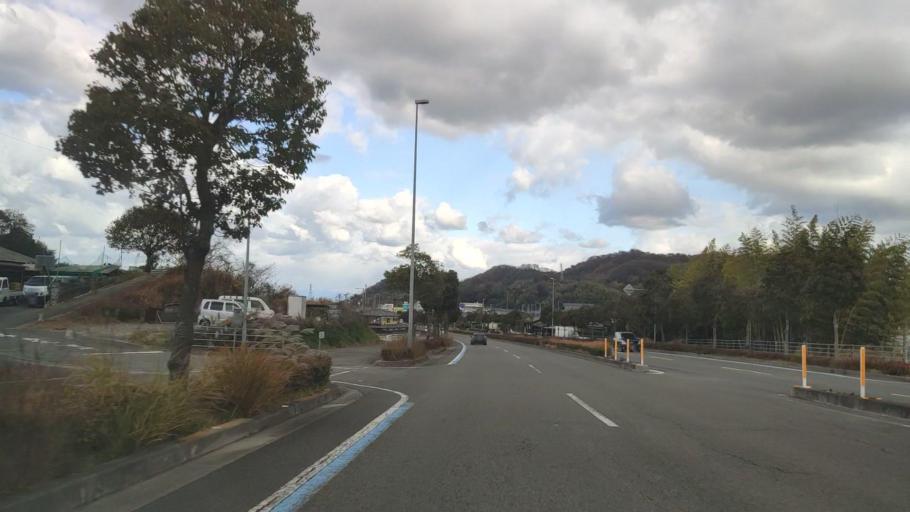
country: JP
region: Ehime
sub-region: Shikoku-chuo Shi
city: Matsuyama
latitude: 33.8953
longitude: 132.7581
